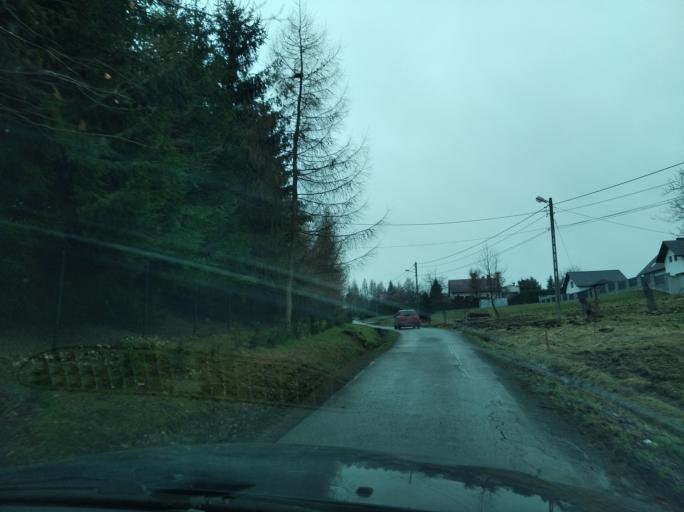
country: PL
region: Subcarpathian Voivodeship
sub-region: Powiat rzeszowski
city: Tyczyn
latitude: 49.9463
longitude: 22.0219
